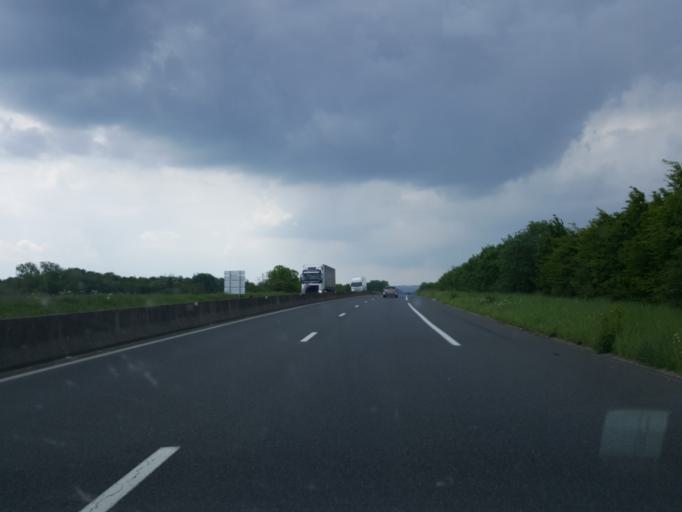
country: FR
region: Picardie
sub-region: Departement de l'Oise
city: Goincourt
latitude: 49.3857
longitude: 2.0657
